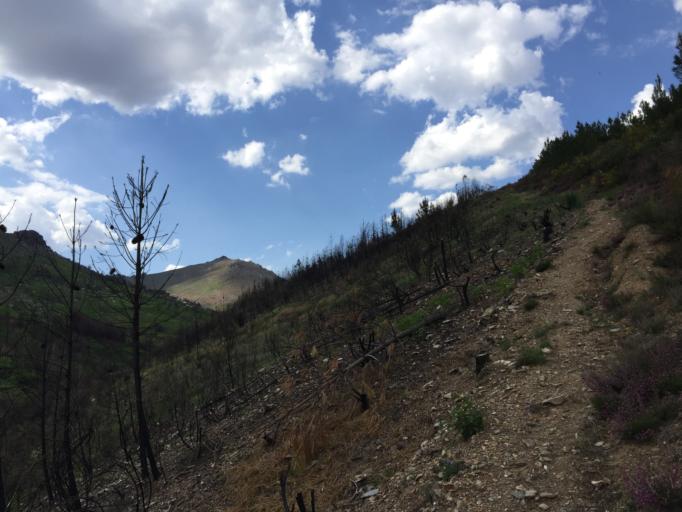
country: PT
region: Coimbra
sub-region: Pampilhosa da Serra
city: Pampilhosa da Serra
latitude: 40.1015
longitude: -7.8657
